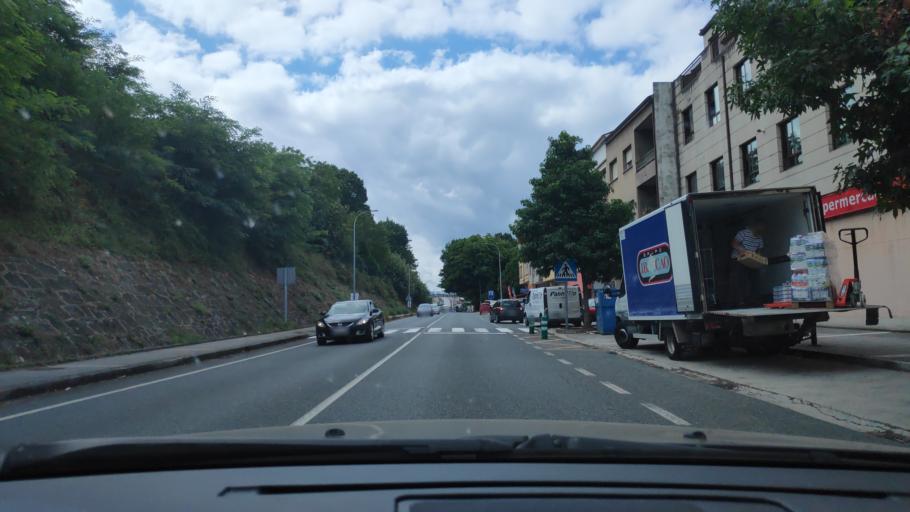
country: ES
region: Galicia
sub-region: Provincia da Coruna
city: Padron
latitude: 42.7229
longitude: -8.6508
